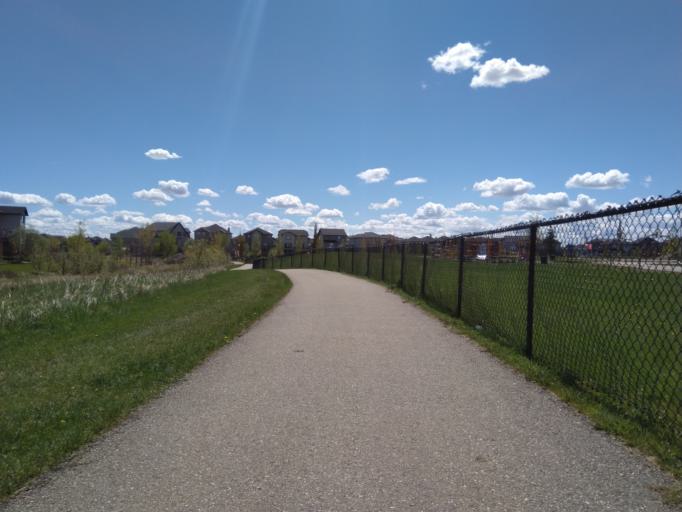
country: CA
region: Alberta
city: Chestermere
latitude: 51.0317
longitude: -113.8381
